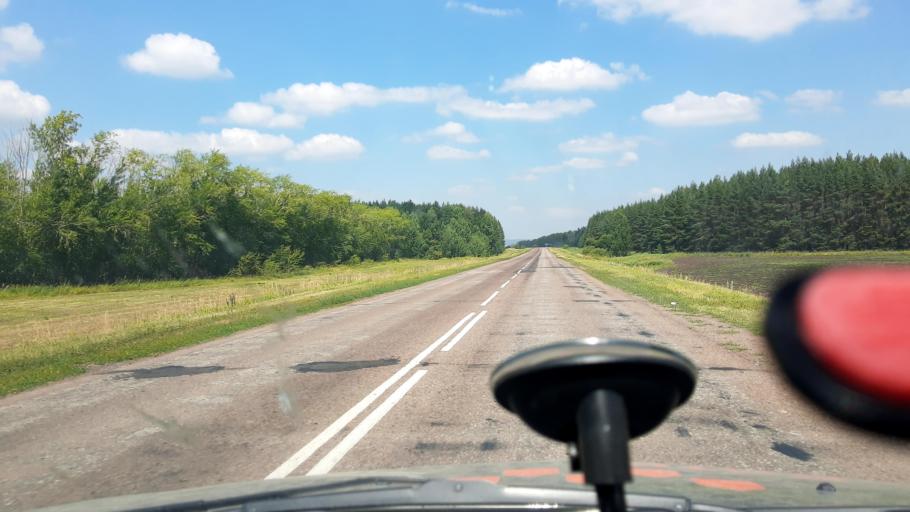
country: RU
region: Bashkortostan
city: Buzdyak
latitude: 54.8358
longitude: 54.5631
